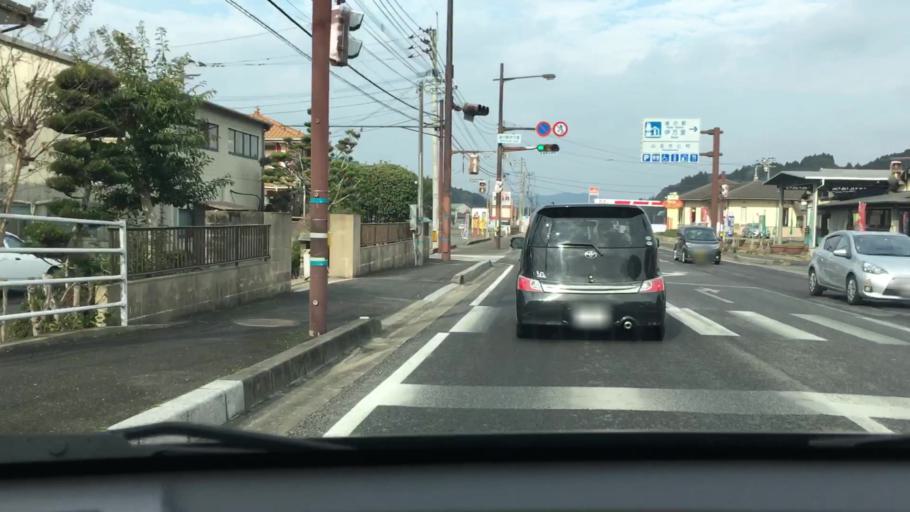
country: JP
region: Saga Prefecture
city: Imaricho-ko
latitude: 33.3133
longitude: 129.9286
